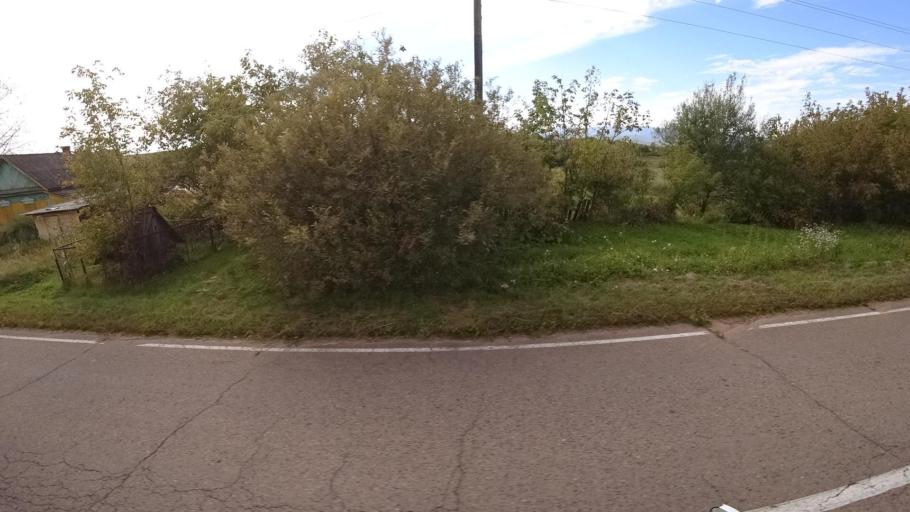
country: RU
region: Primorskiy
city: Dostoyevka
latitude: 44.3241
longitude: 133.4766
